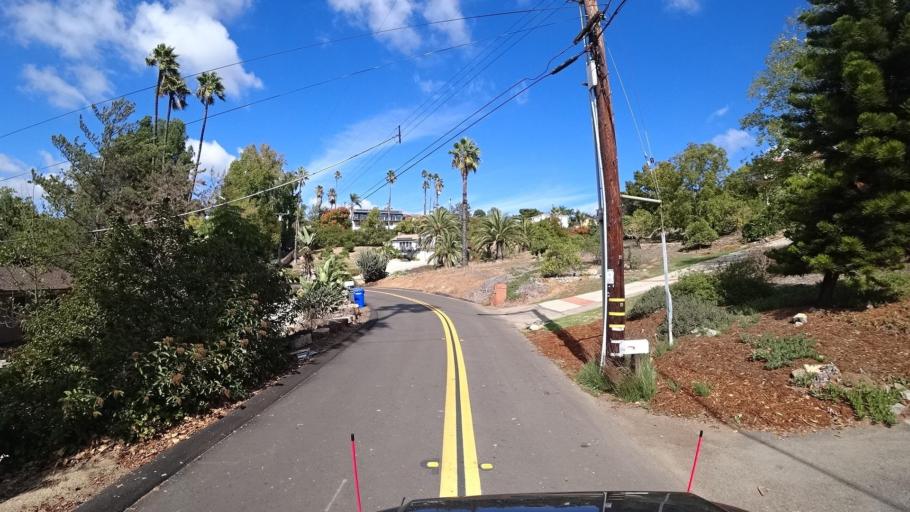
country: US
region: California
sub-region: San Diego County
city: Casa de Oro-Mount Helix
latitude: 32.7598
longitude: -116.9597
